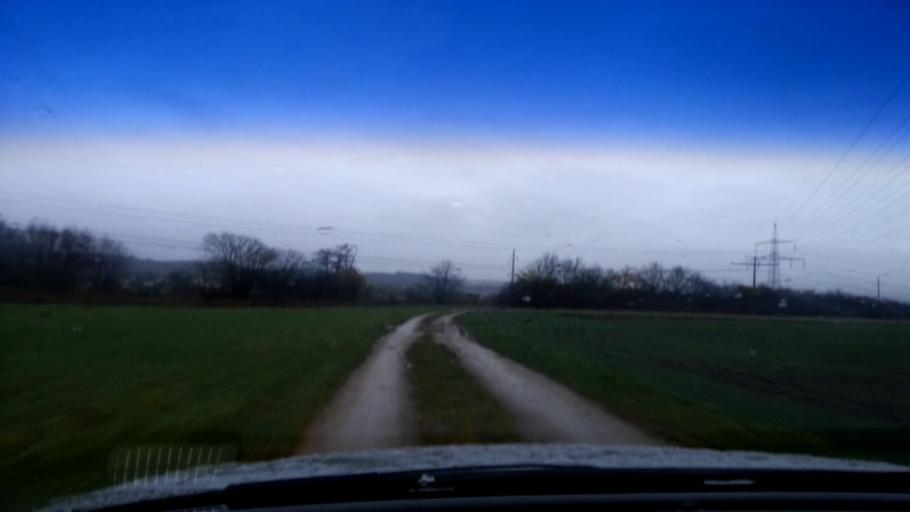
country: DE
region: Bavaria
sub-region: Upper Franconia
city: Viereth-Trunstadt
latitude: 49.9304
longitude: 10.7893
